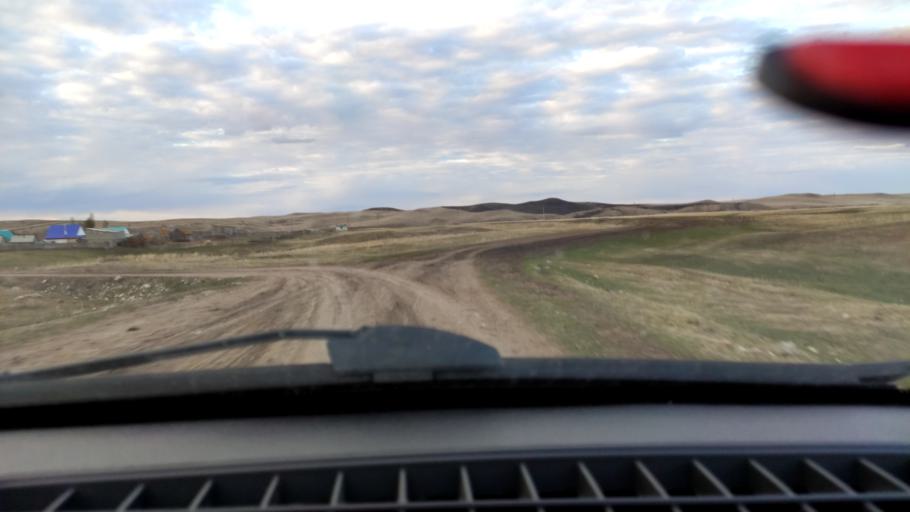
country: RU
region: Bashkortostan
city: Tolbazy
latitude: 54.0160
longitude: 55.5339
